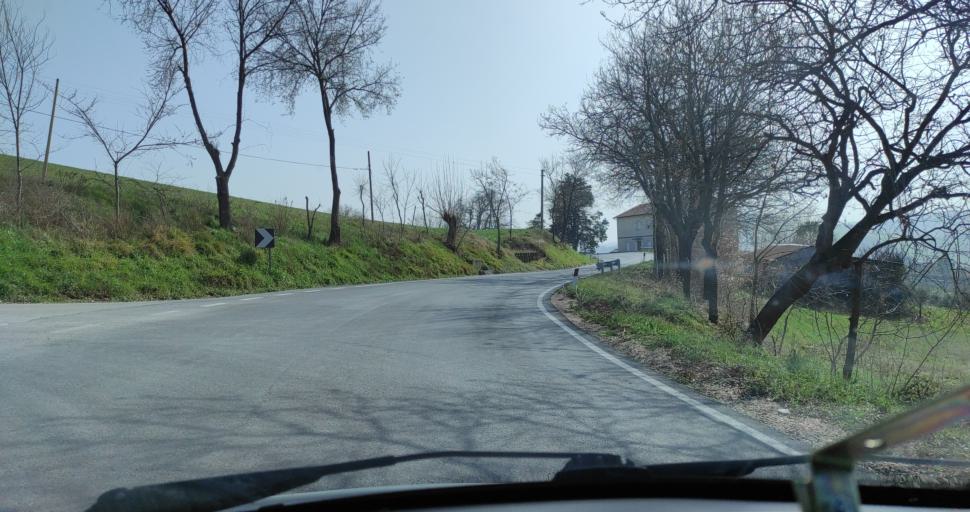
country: IT
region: The Marches
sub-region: Provincia di Macerata
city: Loro Piceno
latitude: 43.1790
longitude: 13.4501
